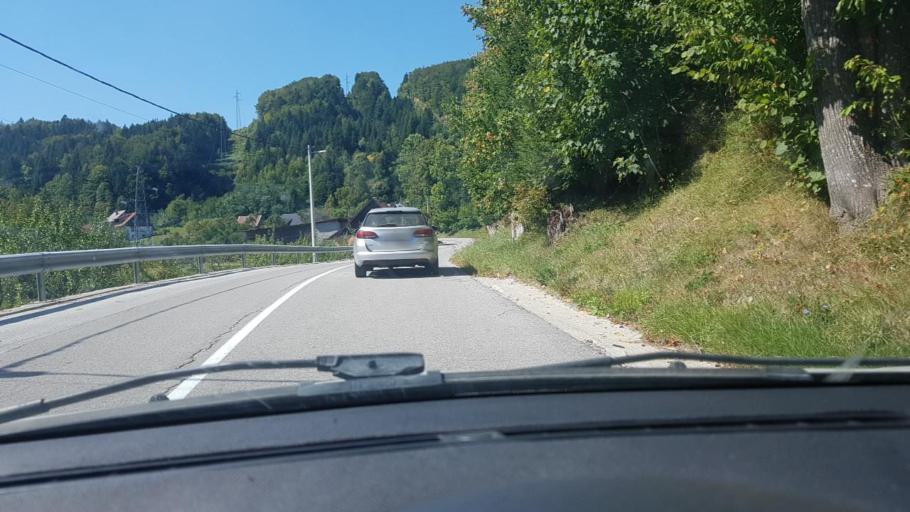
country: HR
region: Primorsko-Goranska
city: Vrbovsko
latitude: 45.3799
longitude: 14.9803
